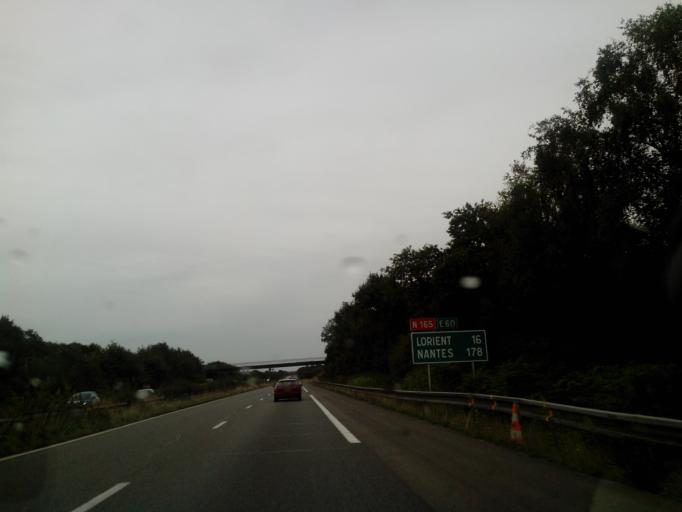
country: FR
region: Brittany
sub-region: Departement du Finistere
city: Redene
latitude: 47.8422
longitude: -3.4981
